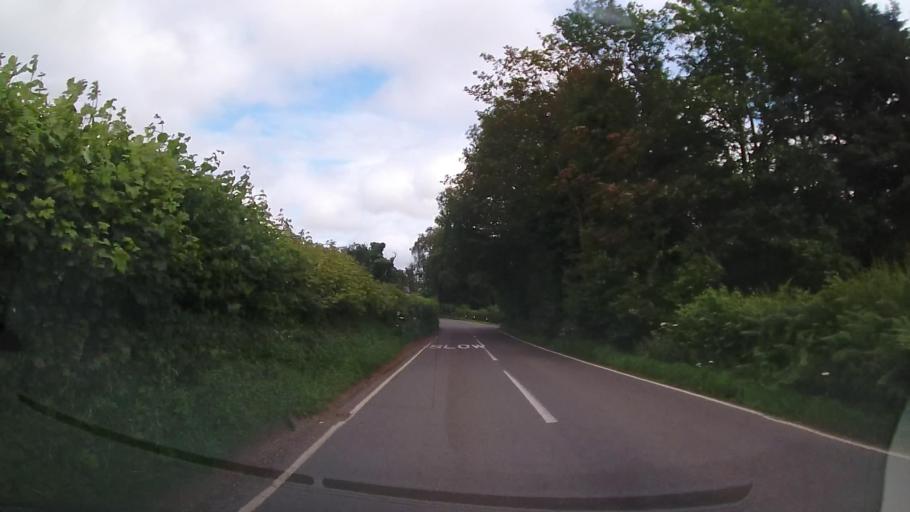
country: GB
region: England
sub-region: Shropshire
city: Pant
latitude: 52.8019
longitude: -3.1351
